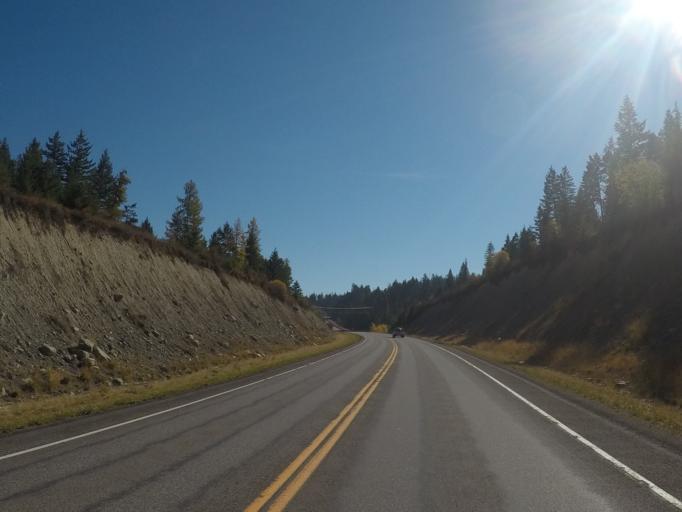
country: US
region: Montana
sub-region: Flathead County
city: Lakeside
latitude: 47.9924
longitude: -114.2080
